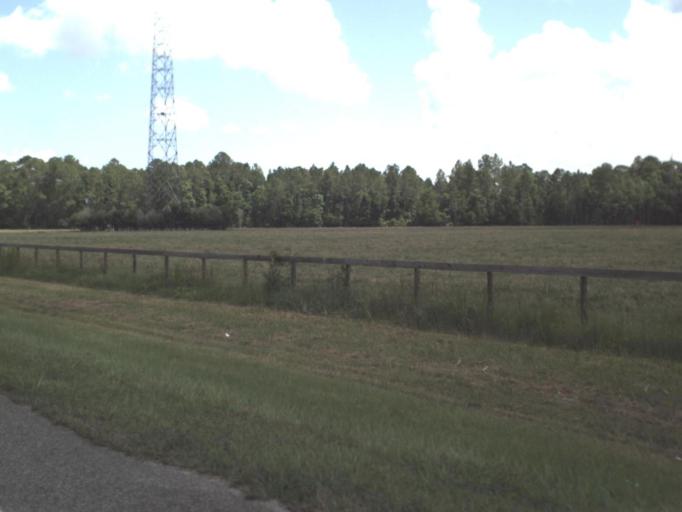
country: US
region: Florida
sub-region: Putnam County
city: East Palatka
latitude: 29.5900
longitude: -81.5662
